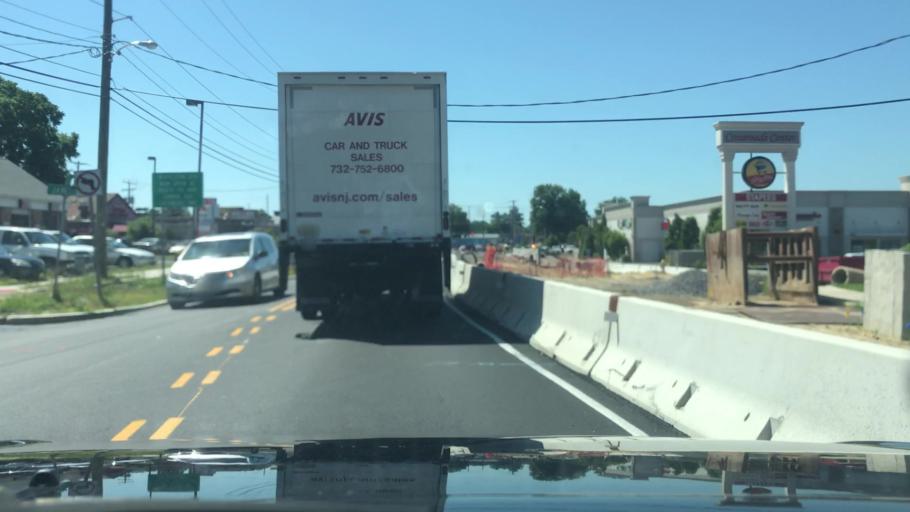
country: US
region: New Jersey
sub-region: Ocean County
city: Toms River
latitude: 39.9662
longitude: -74.2021
